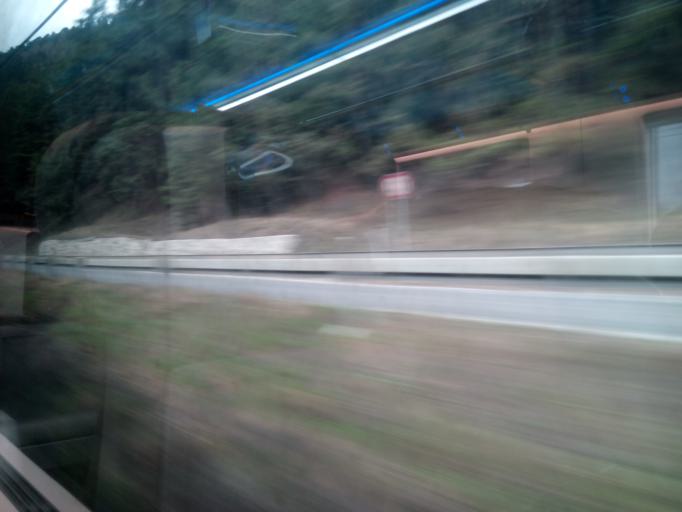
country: SK
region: Zilinsky
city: Ruzomberok
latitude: 49.0849
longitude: 19.3310
